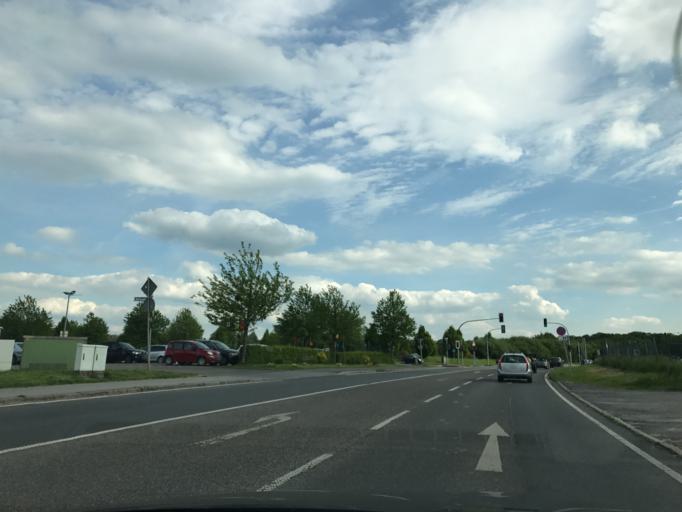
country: DE
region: North Rhine-Westphalia
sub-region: Regierungsbezirk Dusseldorf
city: Muelheim (Ruhr)
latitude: 51.4054
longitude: 6.9507
